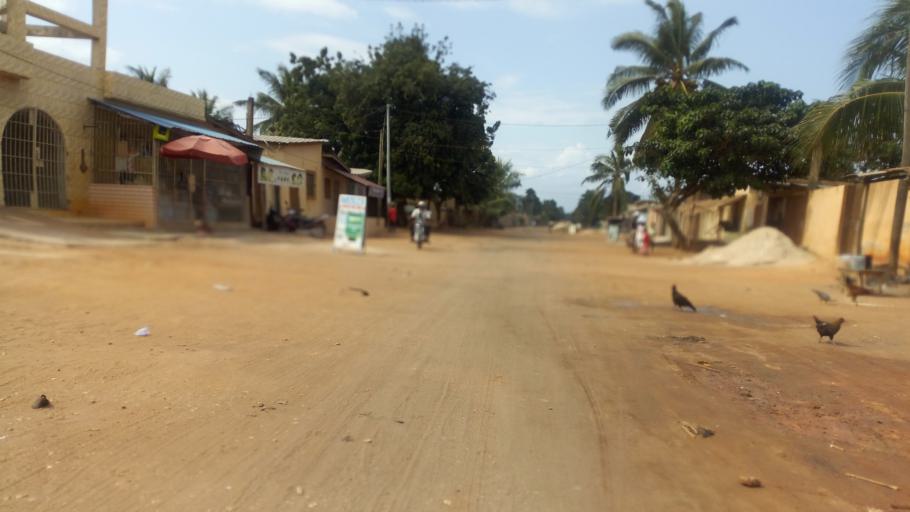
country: TG
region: Maritime
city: Lome
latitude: 6.2276
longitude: 1.1808
